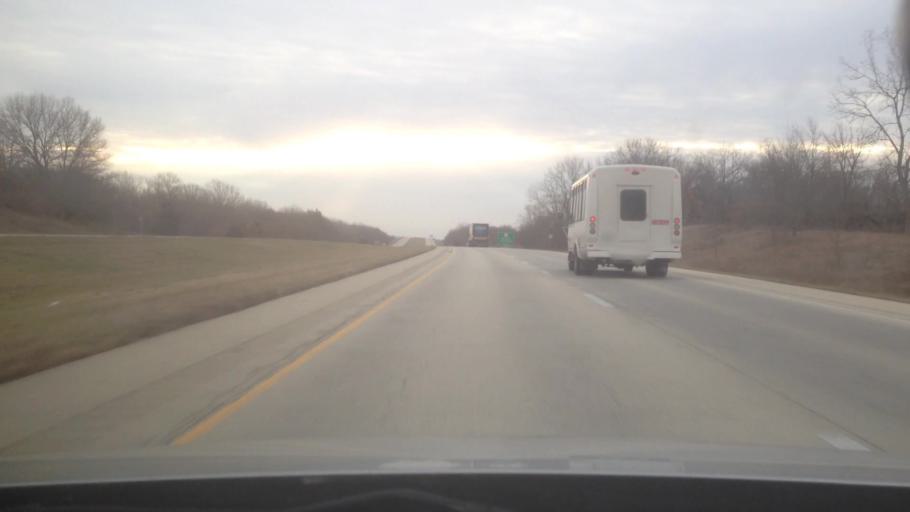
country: US
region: Illinois
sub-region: Macon County
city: Harristown
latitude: 39.8108
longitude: -89.0252
